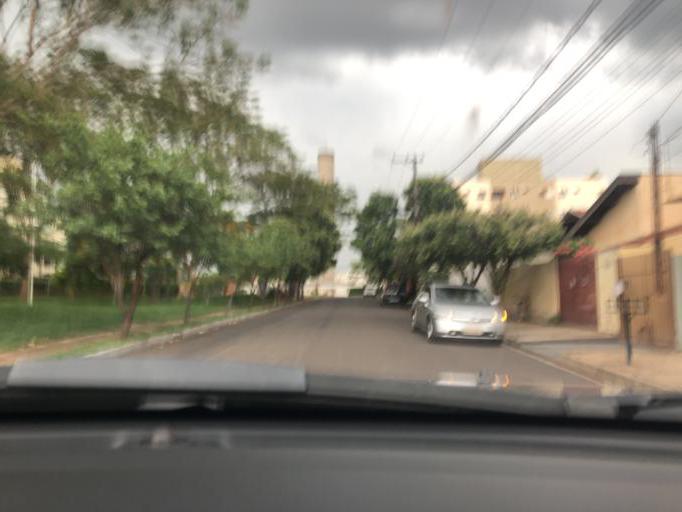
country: BR
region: Sao Paulo
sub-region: Sao Jose Do Rio Preto
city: Sao Jose do Rio Preto
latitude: -20.8403
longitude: -49.3852
